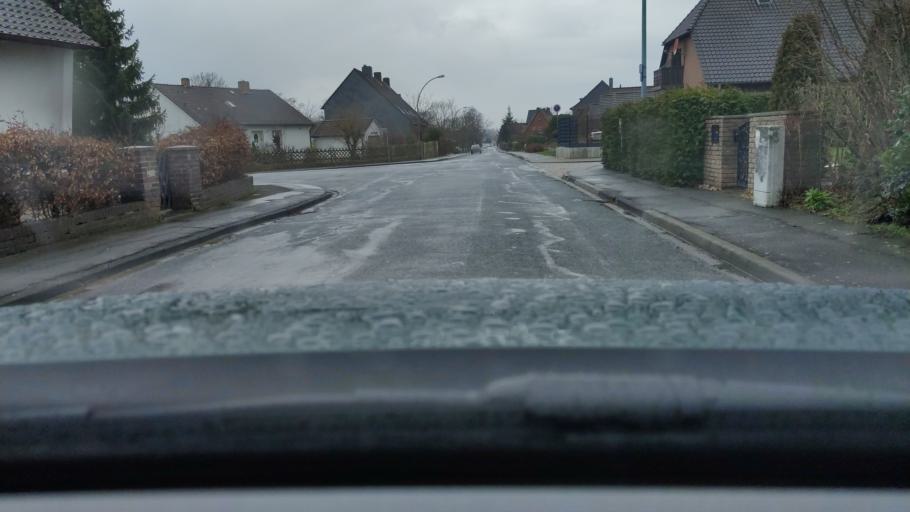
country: DE
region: Lower Saxony
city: Ilsede
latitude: 52.2692
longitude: 10.2296
